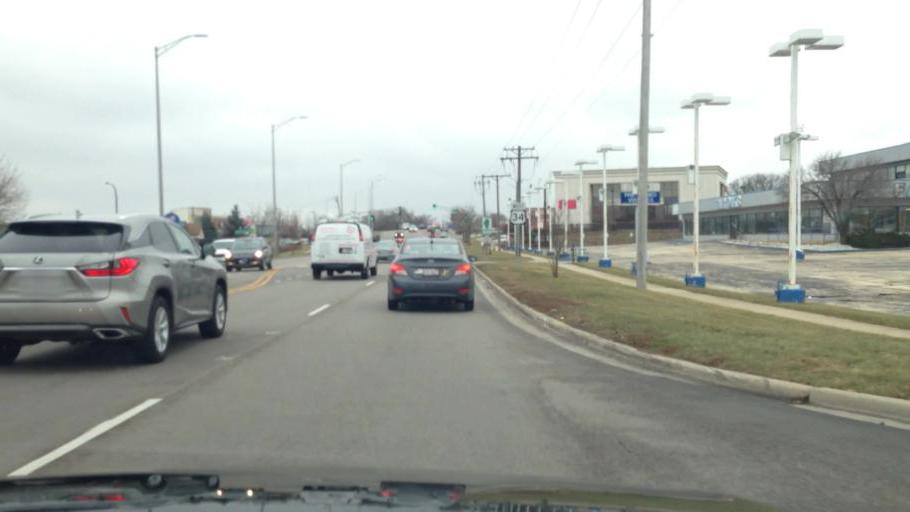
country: US
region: Illinois
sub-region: DuPage County
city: Naperville
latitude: 41.7961
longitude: -88.1193
